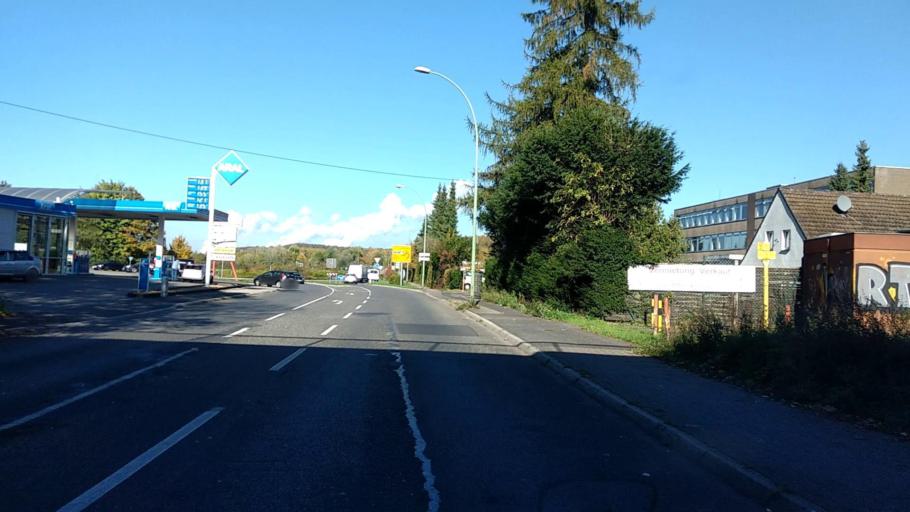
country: DE
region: North Rhine-Westphalia
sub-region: Regierungsbezirk Koln
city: Kerpen
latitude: 50.9239
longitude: 6.7061
